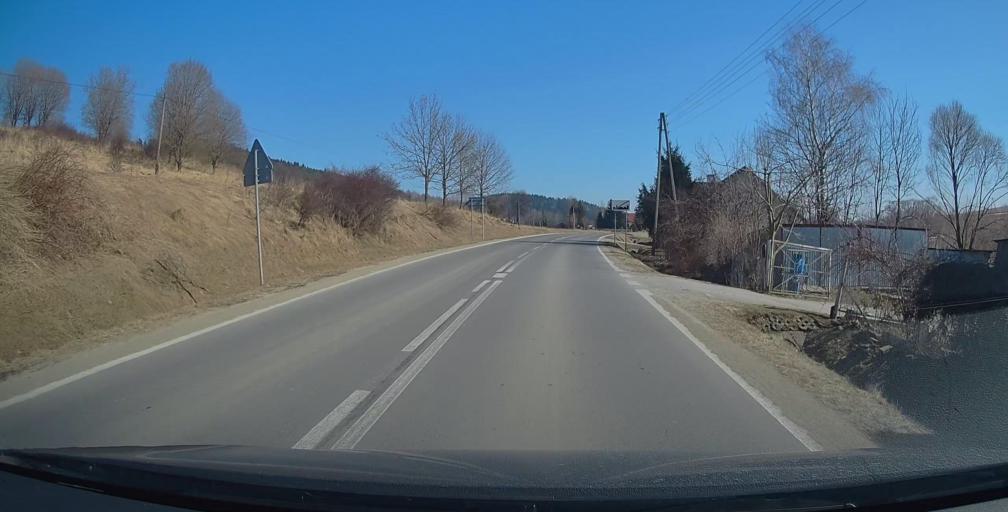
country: PL
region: Subcarpathian Voivodeship
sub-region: Powiat bieszczadzki
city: Ustrzyki Dolne
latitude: 49.4908
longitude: 22.6493
